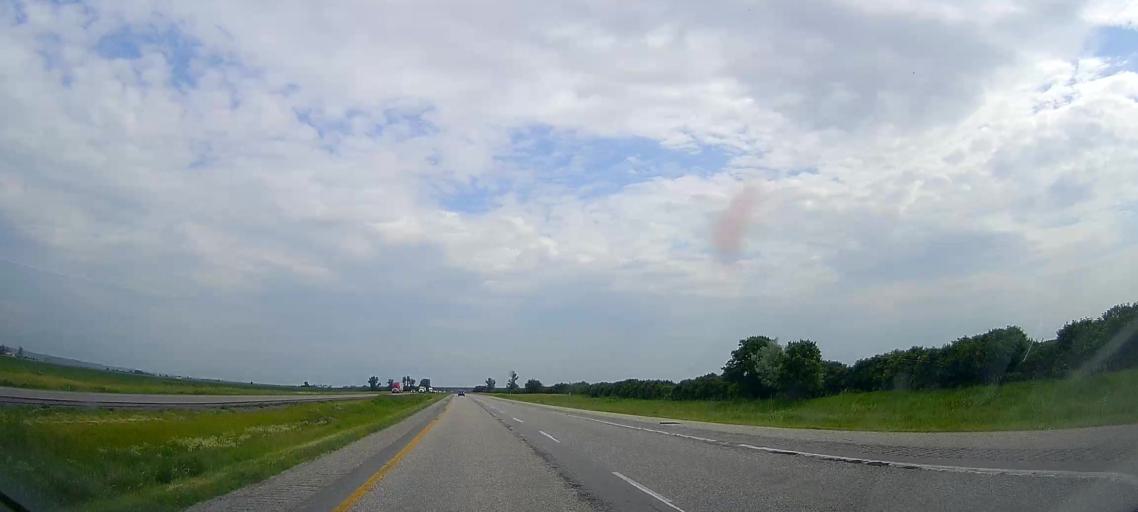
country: US
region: Nebraska
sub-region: Burt County
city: Tekamah
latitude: 41.7841
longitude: -96.0527
